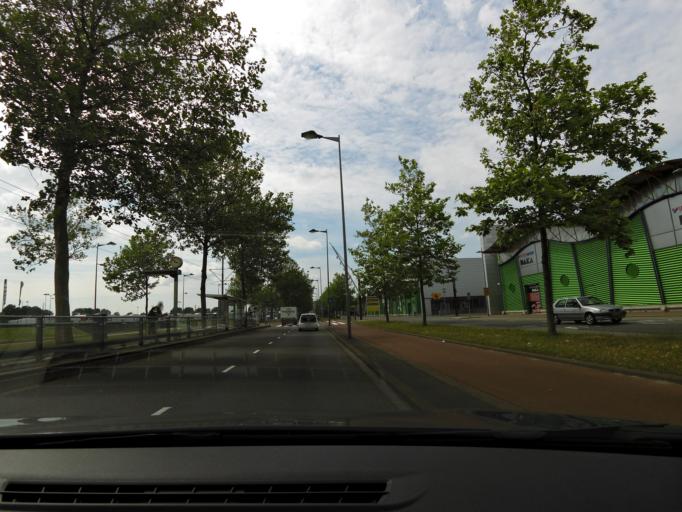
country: NL
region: South Holland
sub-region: Gemeente Rotterdam
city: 's-Gravenland
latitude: 51.8956
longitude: 4.5255
